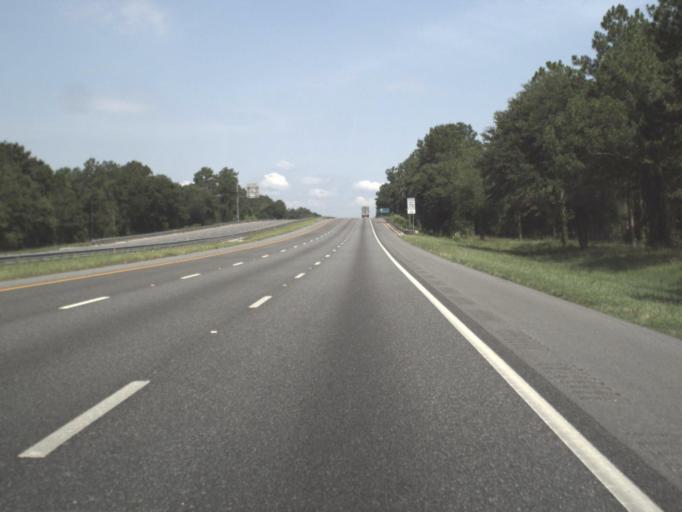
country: US
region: Florida
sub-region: Hamilton County
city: Jasper
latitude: 30.4546
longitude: -82.9425
